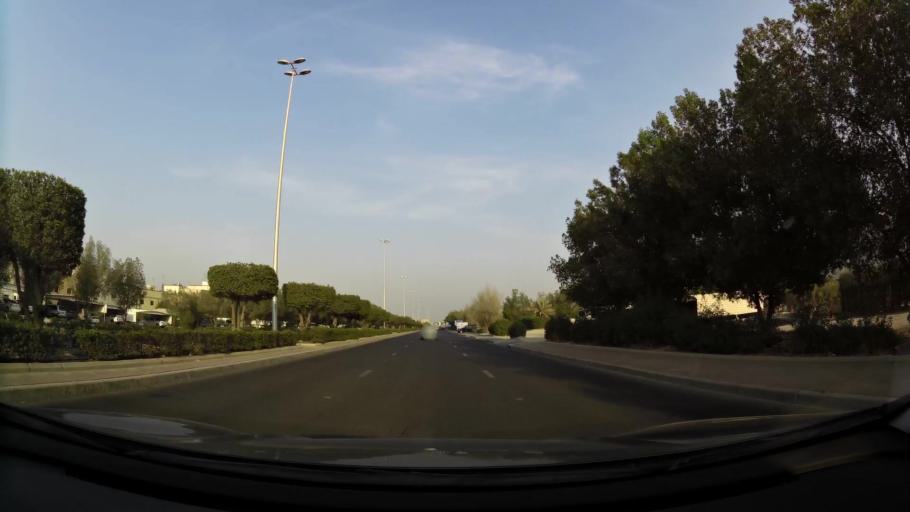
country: KW
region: Mubarak al Kabir
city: Sabah as Salim
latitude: 29.2402
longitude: 48.0559
